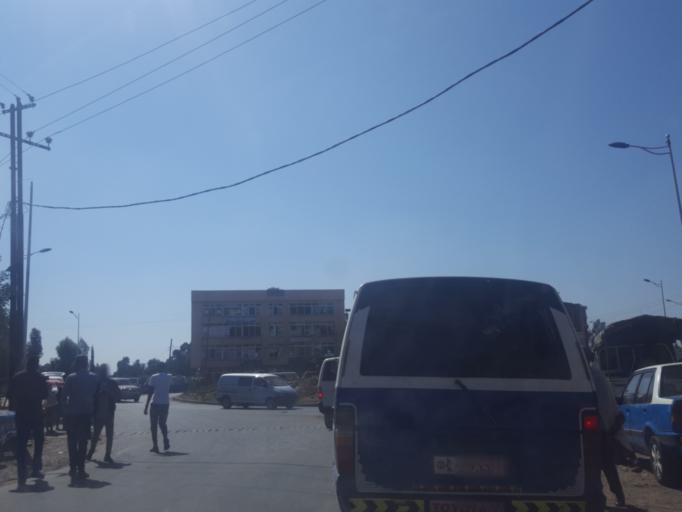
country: ET
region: Adis Abeba
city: Addis Ababa
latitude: 9.0495
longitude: 38.7377
